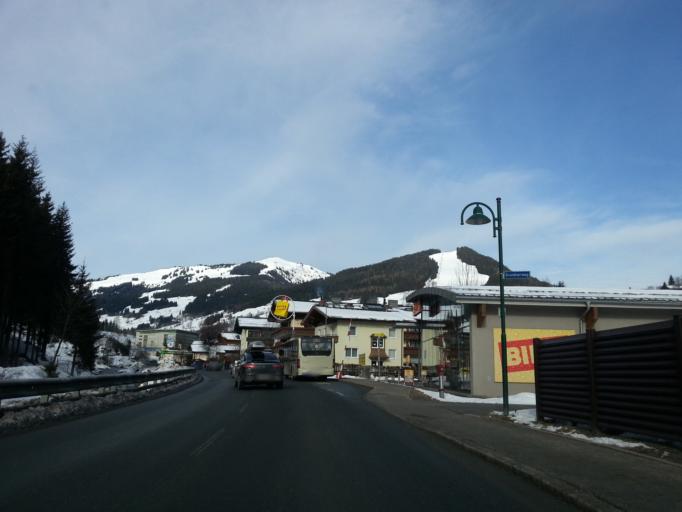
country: AT
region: Salzburg
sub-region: Politischer Bezirk Zell am See
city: Saalbach
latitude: 47.3884
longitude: 12.6458
